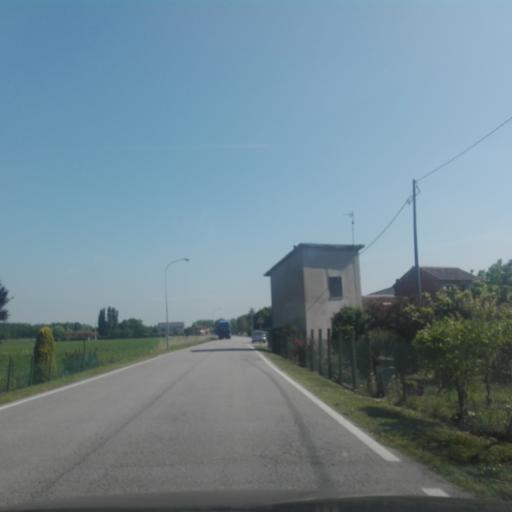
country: IT
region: Veneto
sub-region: Provincia di Rovigo
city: Gavello
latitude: 45.0295
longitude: 11.9175
